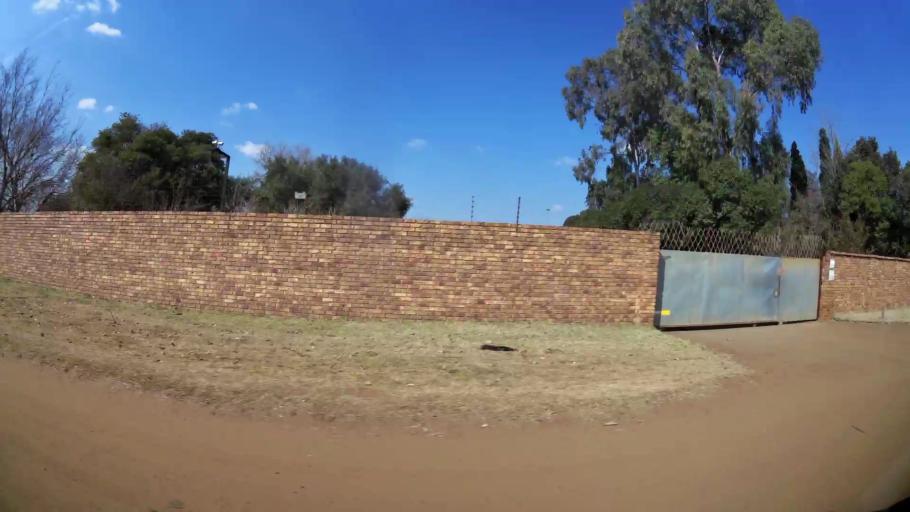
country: ZA
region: Gauteng
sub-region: Ekurhuleni Metropolitan Municipality
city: Benoni
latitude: -26.1055
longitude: 28.4014
